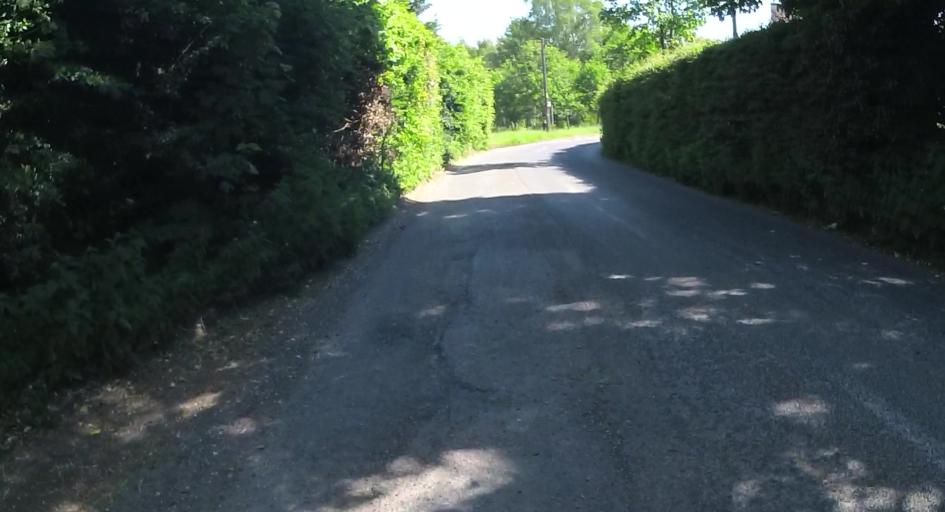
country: GB
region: England
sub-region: Hampshire
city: Hook
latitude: 51.3098
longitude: -0.9839
